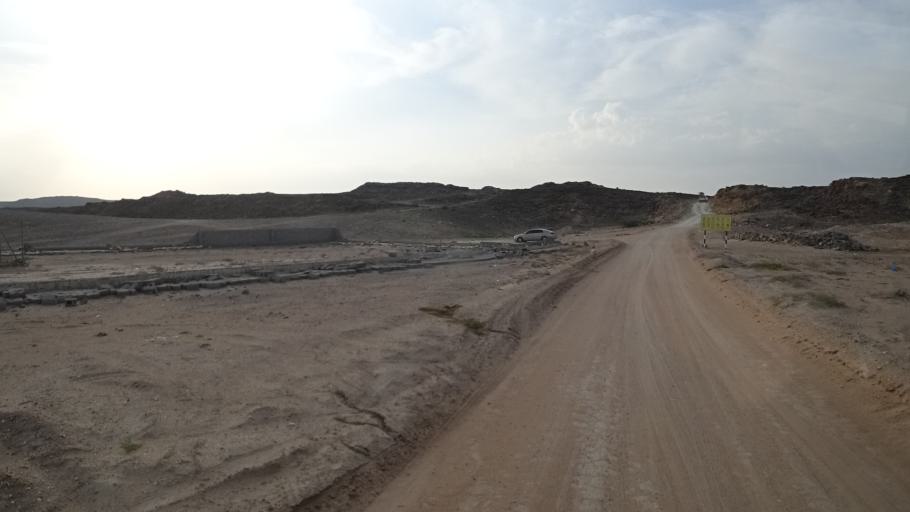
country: OM
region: Ash Sharqiyah
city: Sur
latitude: 22.4504
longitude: 59.8257
